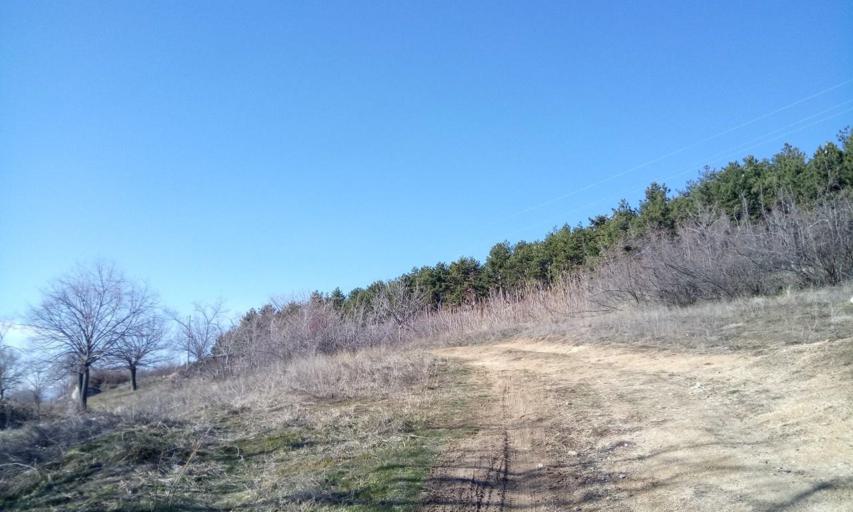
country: BG
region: Plovdiv
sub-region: Obshtina Khisarya
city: Khisarya
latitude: 42.5250
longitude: 24.7185
